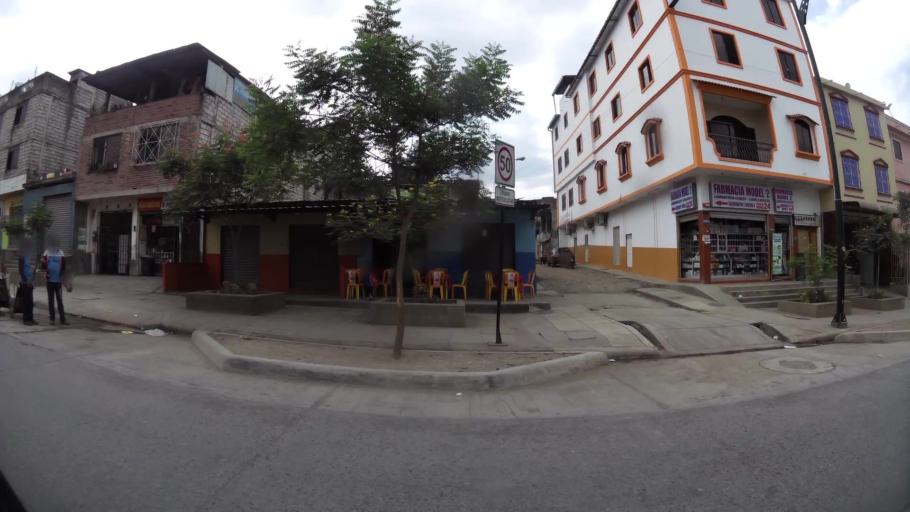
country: EC
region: Guayas
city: Santa Lucia
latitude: -2.1036
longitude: -79.9501
